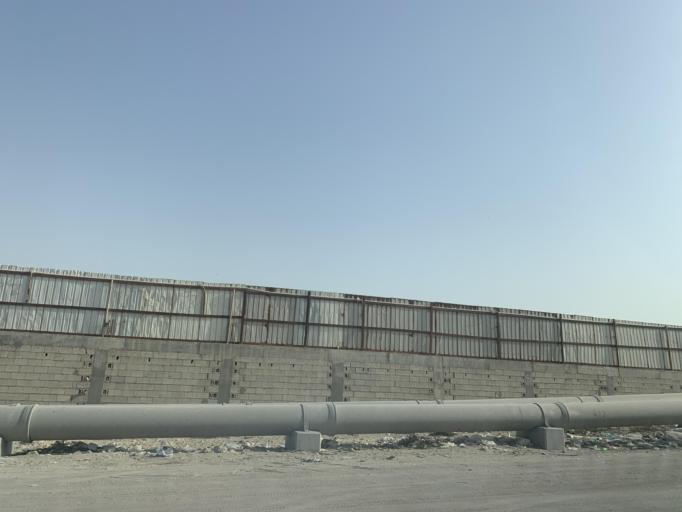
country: BH
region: Central Governorate
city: Madinat Hamad
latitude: 26.1441
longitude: 50.4822
